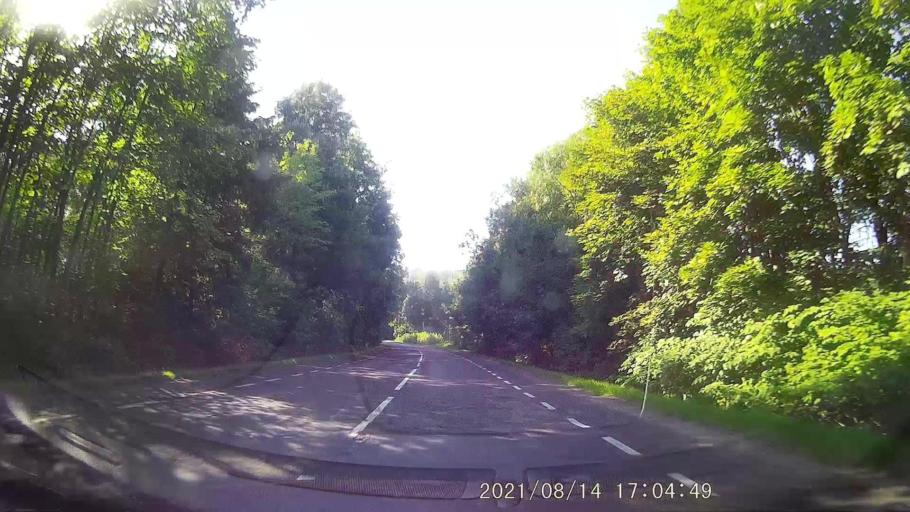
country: PL
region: Lower Silesian Voivodeship
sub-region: Powiat jeleniogorski
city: Kowary
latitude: 50.8041
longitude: 15.8359
